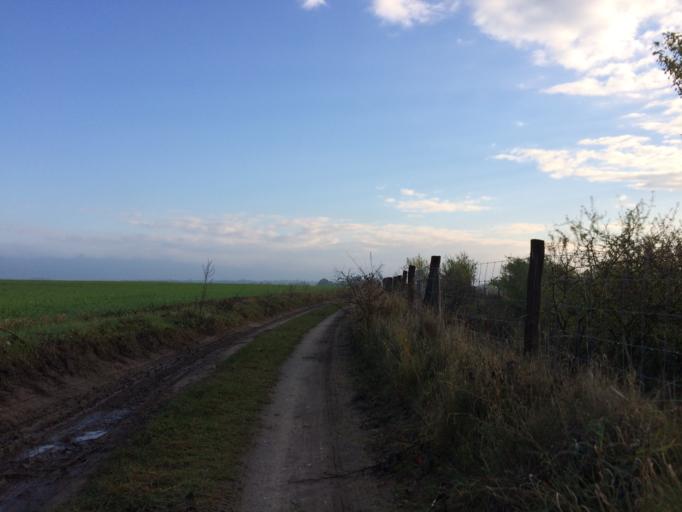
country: DK
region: Zealand
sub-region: Ringsted Kommune
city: Ringsted
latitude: 55.4881
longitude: 11.7523
